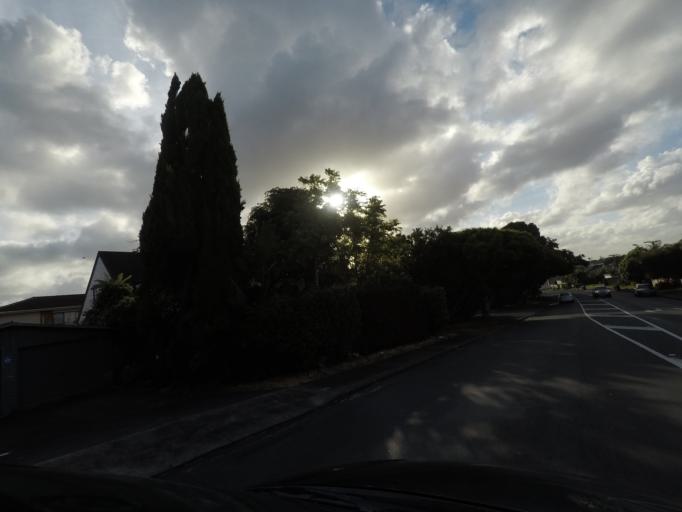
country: NZ
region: Auckland
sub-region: Auckland
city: Auckland
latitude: -36.9153
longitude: 174.7589
